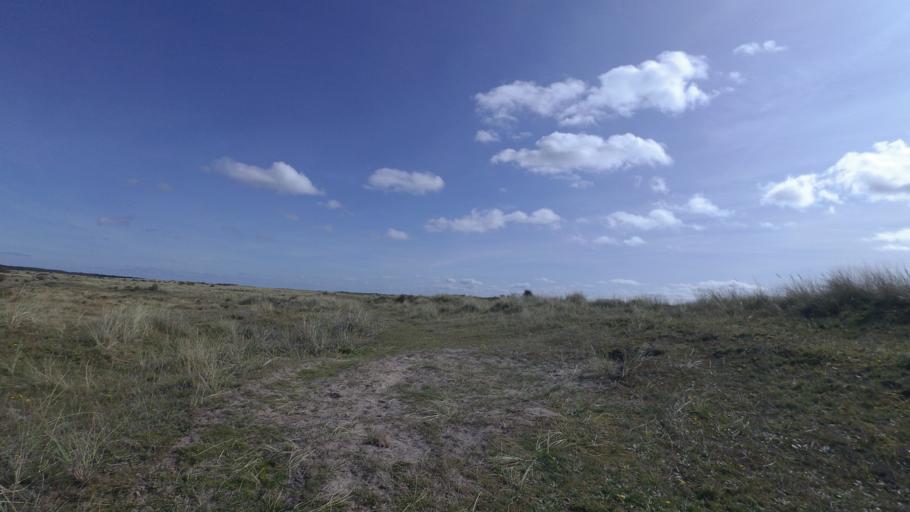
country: NL
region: Friesland
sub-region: Gemeente Ameland
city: Nes
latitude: 53.4503
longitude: 5.7333
